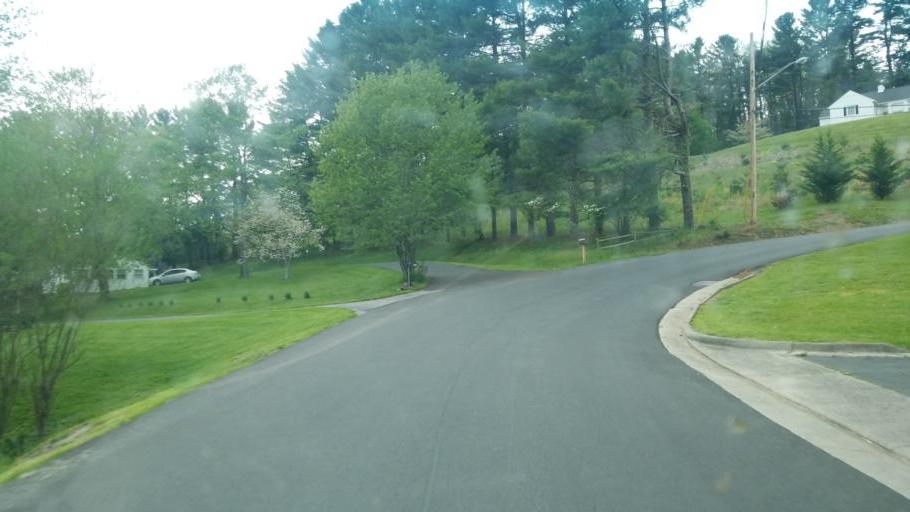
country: US
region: Virginia
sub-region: Smyth County
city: Marion
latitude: 36.8507
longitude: -81.4969
